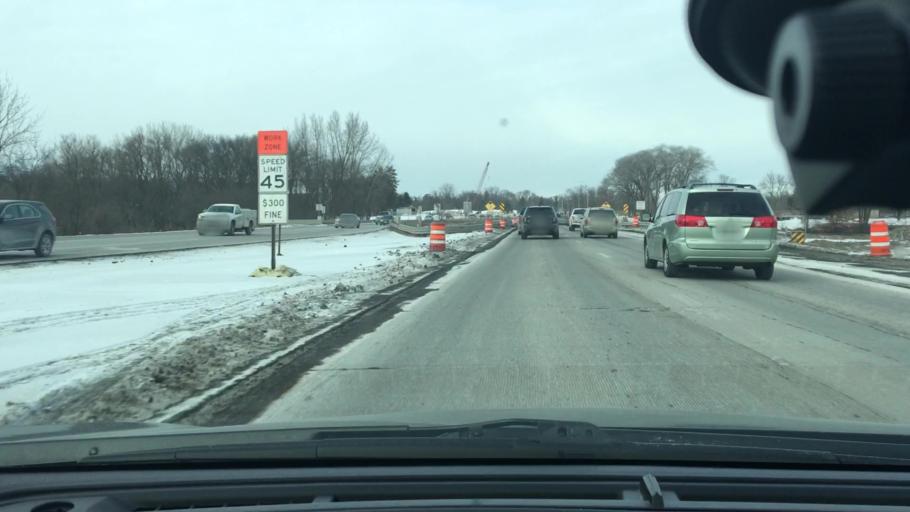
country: US
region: Minnesota
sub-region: Hennepin County
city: Champlin
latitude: 45.1811
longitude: -93.3921
